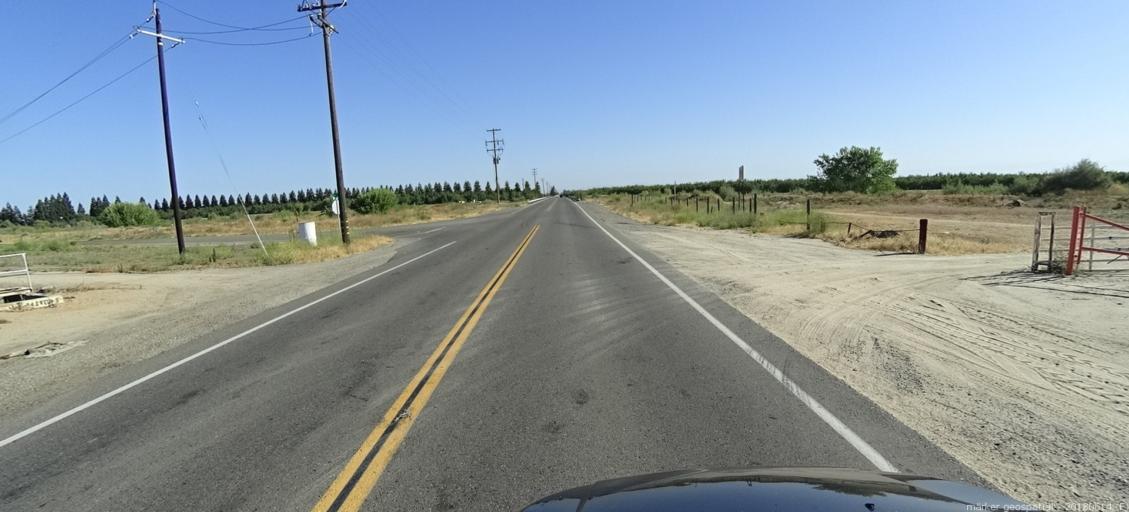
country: US
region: California
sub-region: Madera County
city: Madera
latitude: 36.9661
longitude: -120.1285
